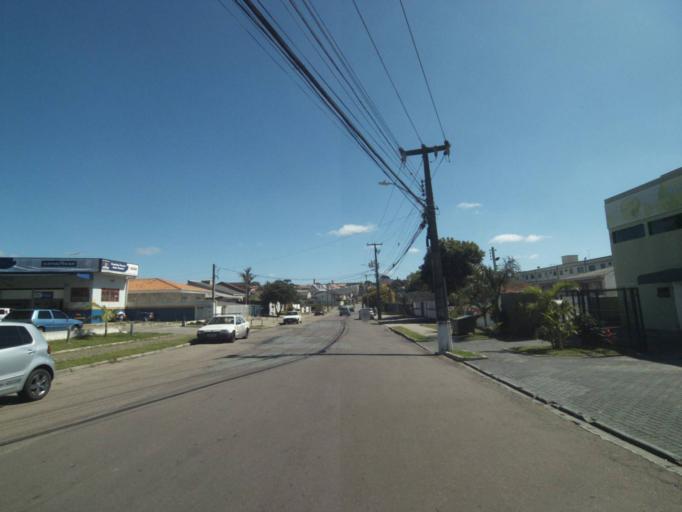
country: BR
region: Parana
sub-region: Pinhais
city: Pinhais
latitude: -25.4370
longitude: -49.2279
